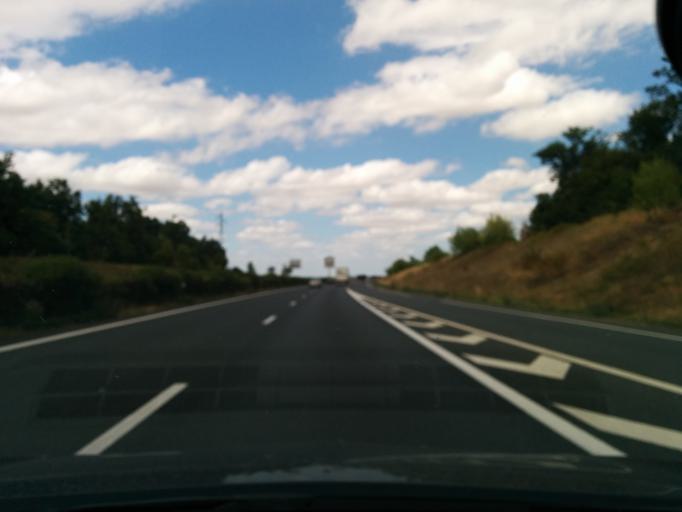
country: FR
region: Centre
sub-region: Departement de l'Indre
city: Saint-Maur
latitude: 46.7969
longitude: 1.6176
